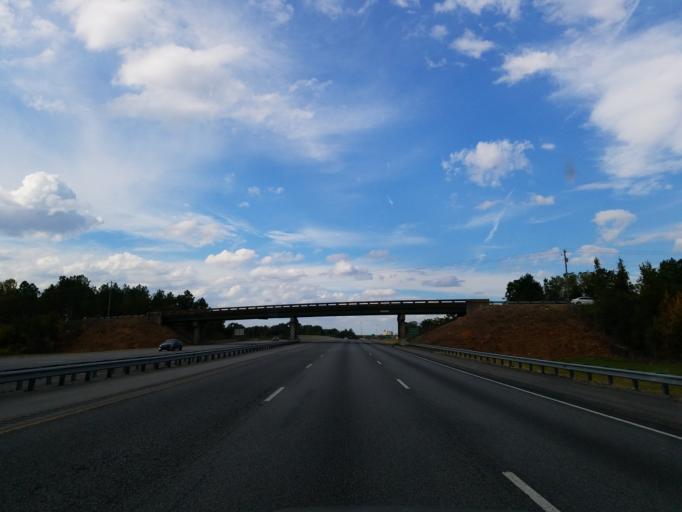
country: US
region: Georgia
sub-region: Crisp County
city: Cordele
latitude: 31.9248
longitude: -83.7449
